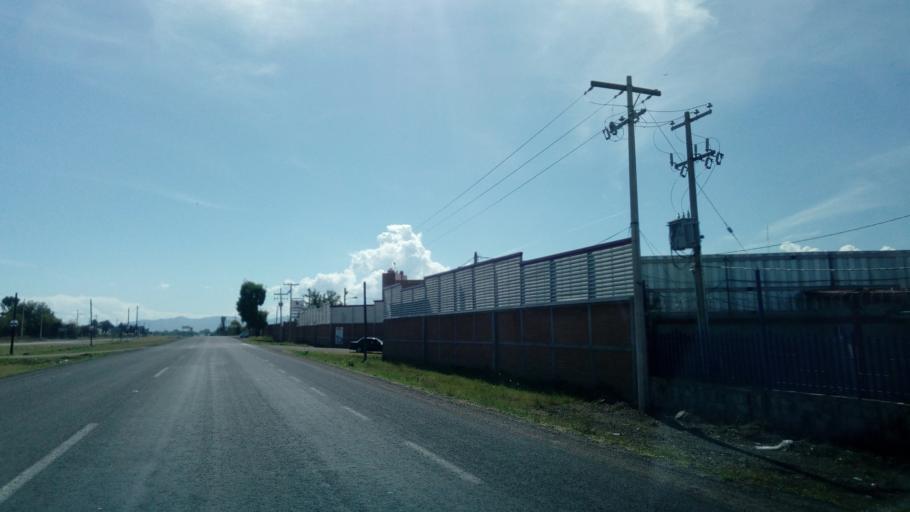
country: MX
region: Durango
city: Victoria de Durango
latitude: 24.0843
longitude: -104.5605
